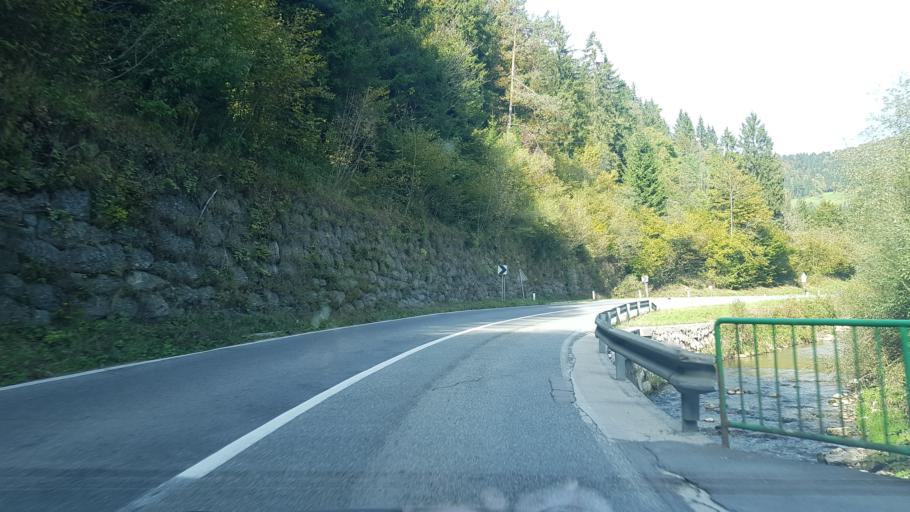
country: SI
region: Dobrna
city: Dobrna
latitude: 46.4044
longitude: 15.1789
